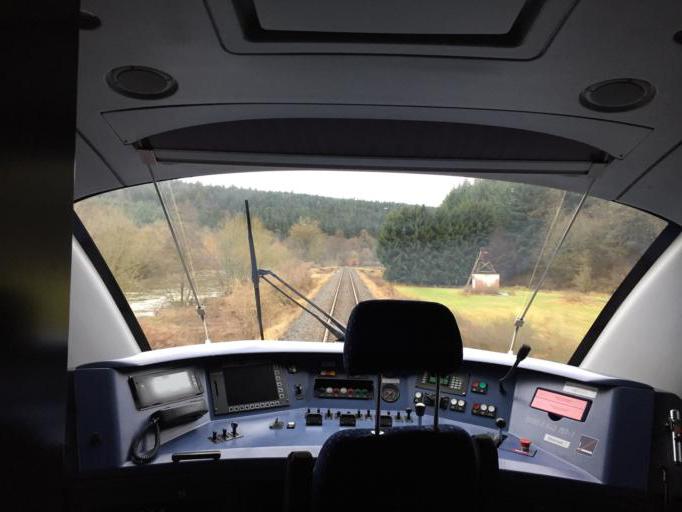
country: DE
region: Hesse
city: Frankenberg
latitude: 51.0923
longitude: 8.8319
